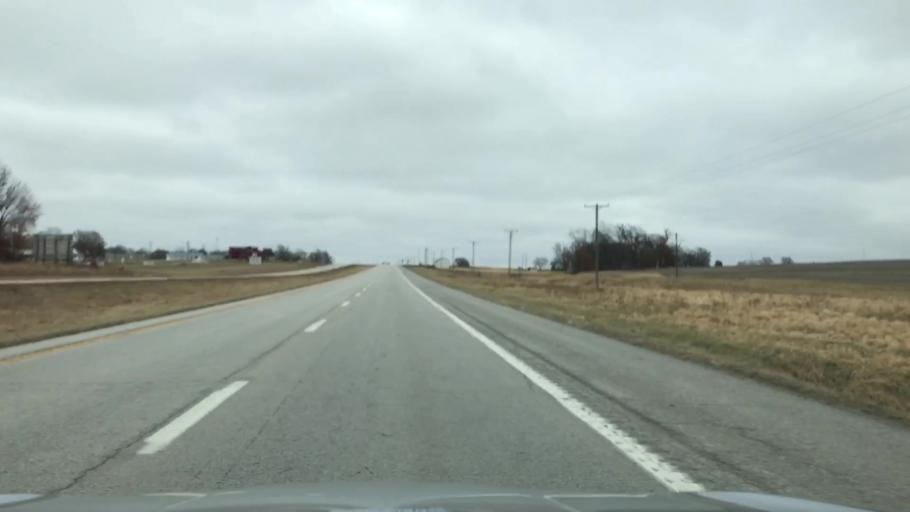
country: US
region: Missouri
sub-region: Livingston County
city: Chillicothe
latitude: 39.7753
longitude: -93.5267
